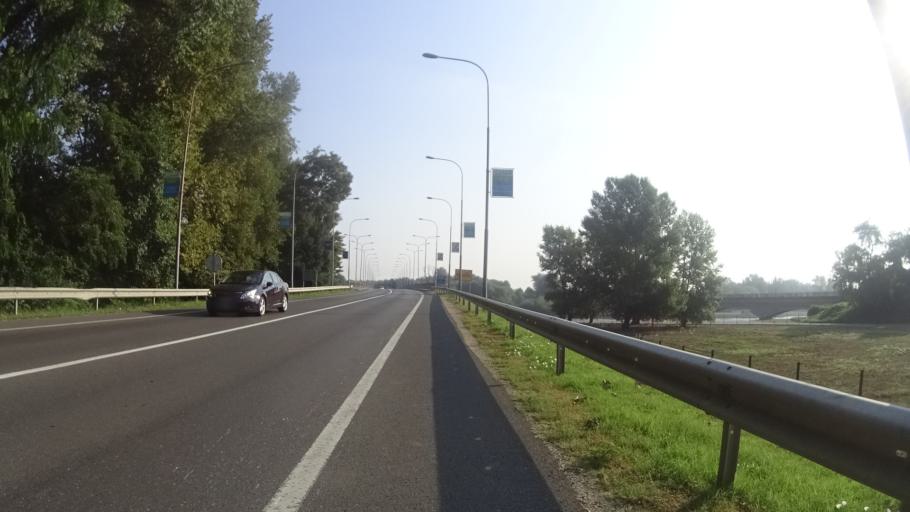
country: HR
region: Varazdinska
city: Varazdin
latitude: 46.3204
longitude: 16.3569
